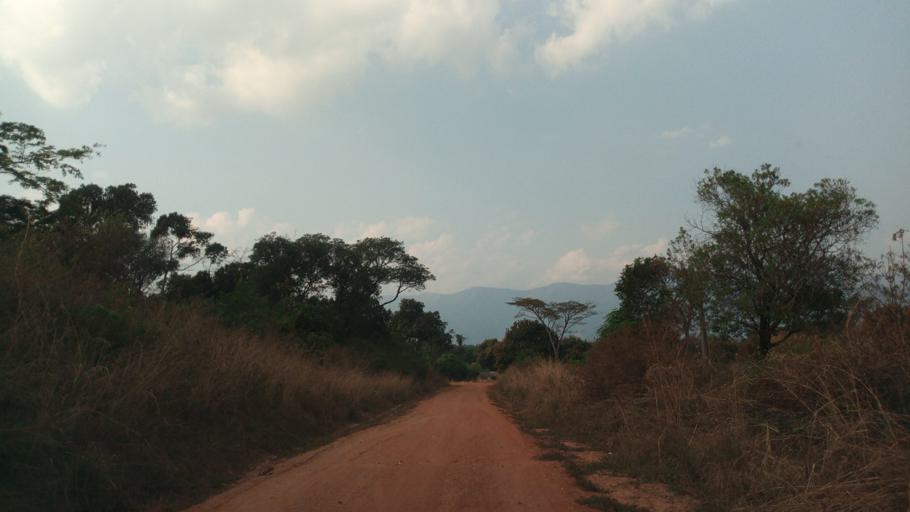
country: TZ
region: Kigoma
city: Kigoma
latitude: -5.1623
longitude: 28.9021
